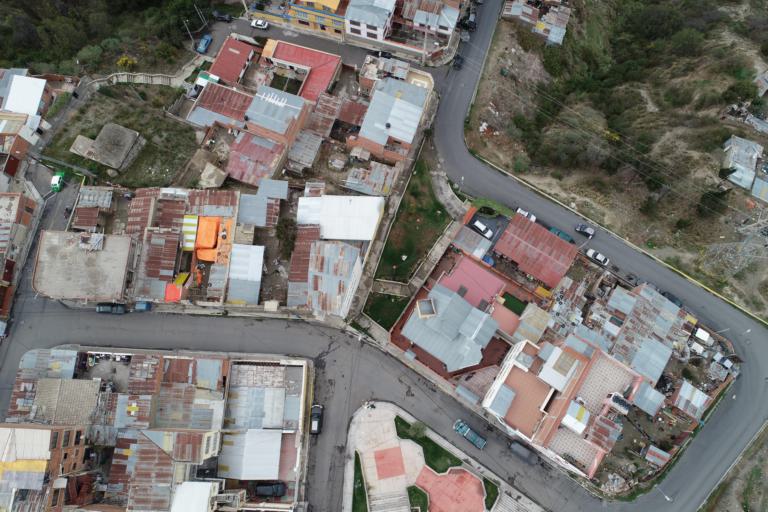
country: BO
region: La Paz
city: La Paz
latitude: -16.5141
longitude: -68.1084
